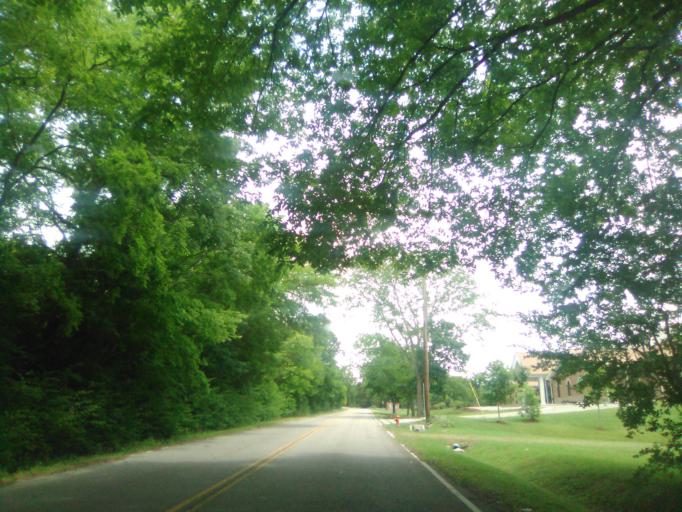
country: US
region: Tennessee
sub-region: Davidson County
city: Belle Meade
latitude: 36.1320
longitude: -86.8942
